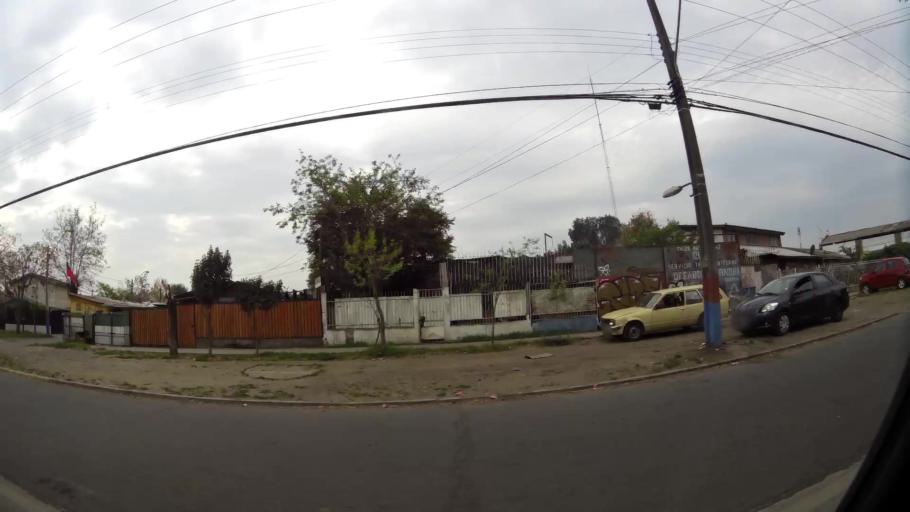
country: CL
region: Santiago Metropolitan
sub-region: Provincia de Santiago
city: Lo Prado
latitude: -33.5004
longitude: -70.7664
